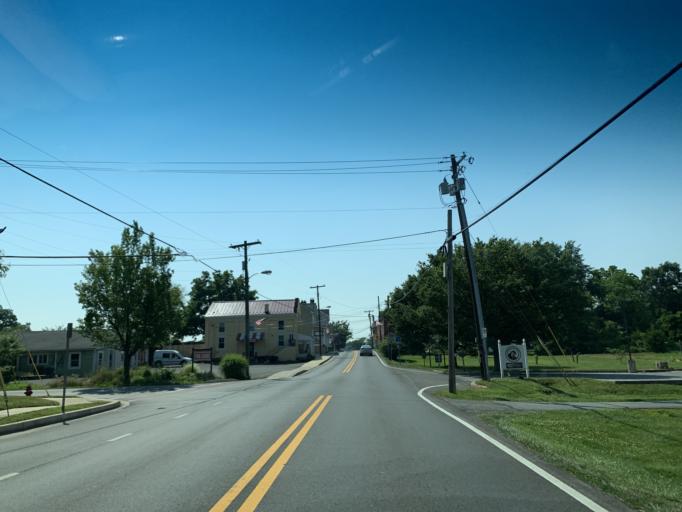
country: US
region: Maryland
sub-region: Montgomery County
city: Poolesville
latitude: 39.1454
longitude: -77.4144
